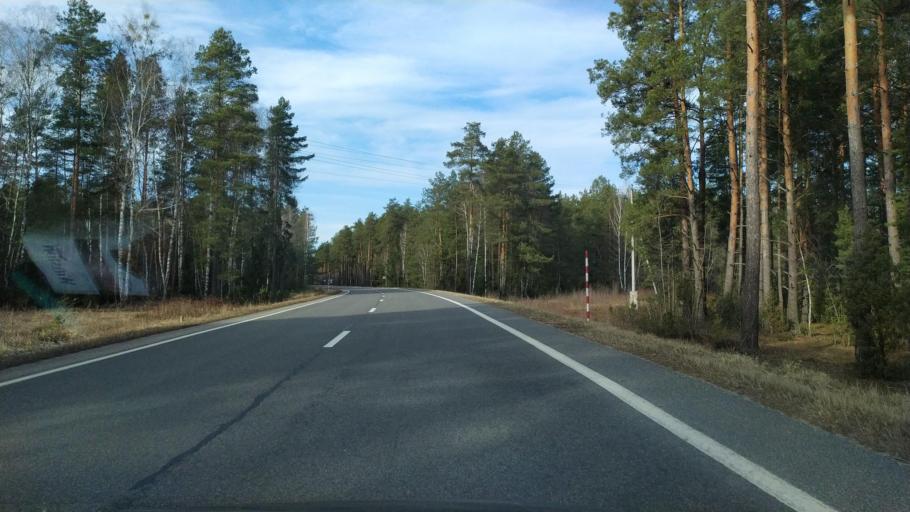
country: BY
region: Brest
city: Pruzhany
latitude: 52.5200
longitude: 24.1777
